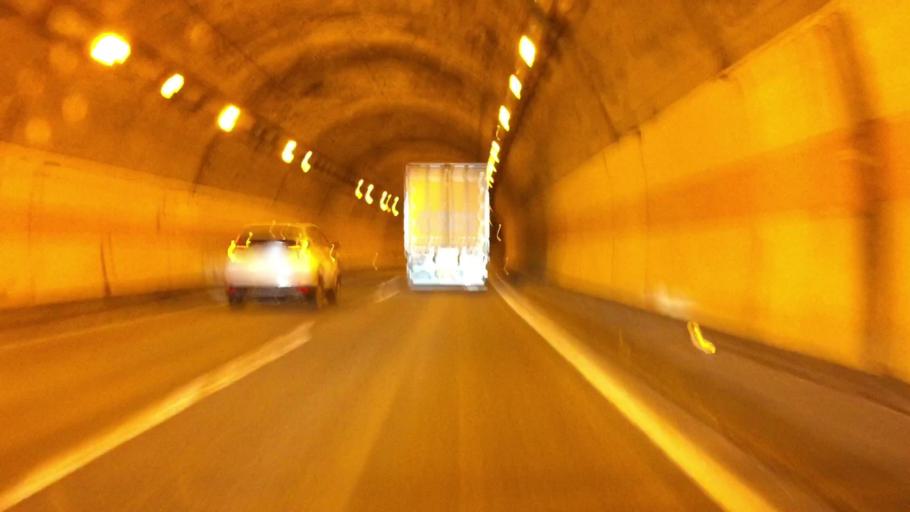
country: JP
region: Gunma
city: Numata
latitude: 36.7227
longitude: 138.9755
